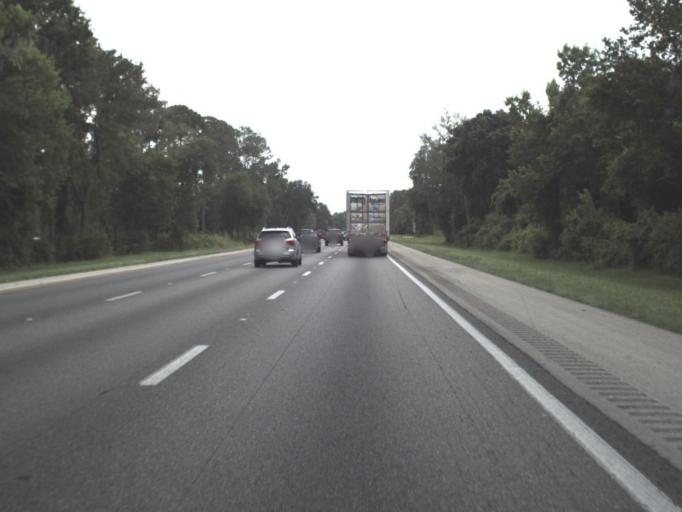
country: US
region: Florida
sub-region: Alachua County
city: Gainesville
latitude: 29.5473
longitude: -82.3361
